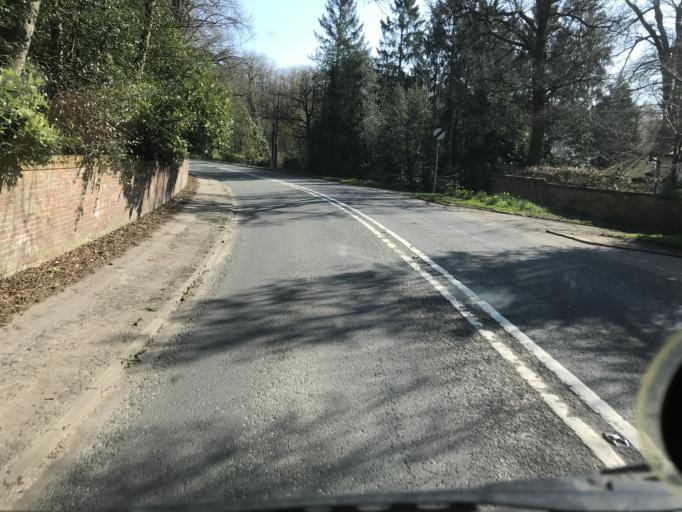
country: GB
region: England
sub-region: Cheshire East
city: Knutsford
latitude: 53.2885
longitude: -2.3463
